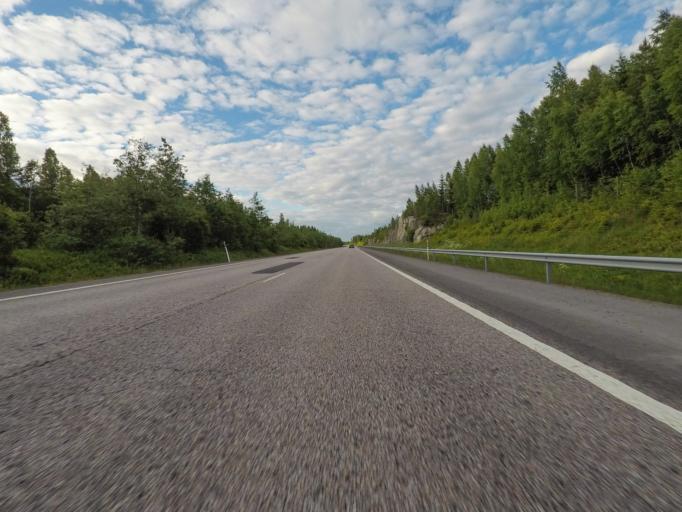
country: FI
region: Paijanne Tavastia
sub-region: Lahti
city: Lahti
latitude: 60.8806
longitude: 25.5830
